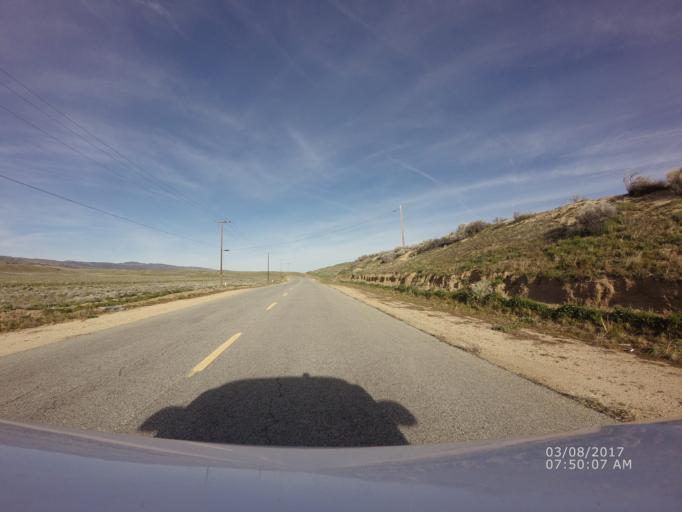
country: US
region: California
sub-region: Los Angeles County
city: Green Valley
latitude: 34.7158
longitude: -118.3618
